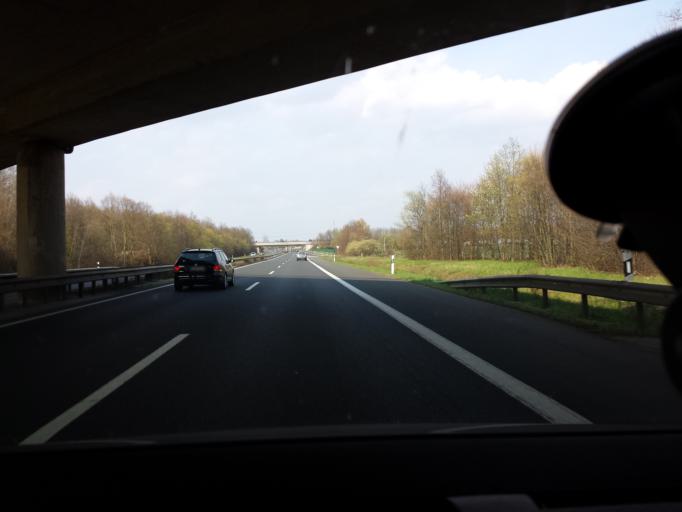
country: DE
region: Lower Saxony
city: Leiferde
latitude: 52.1999
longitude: 10.5279
